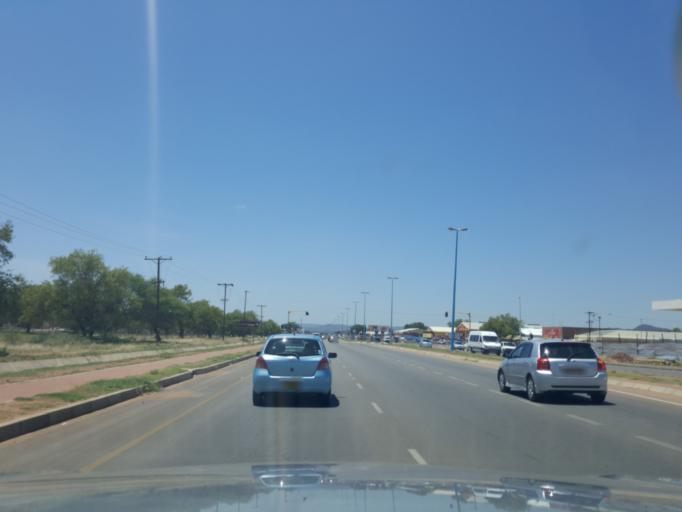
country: BW
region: Kweneng
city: Mogoditshane
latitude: -24.6110
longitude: 25.8605
